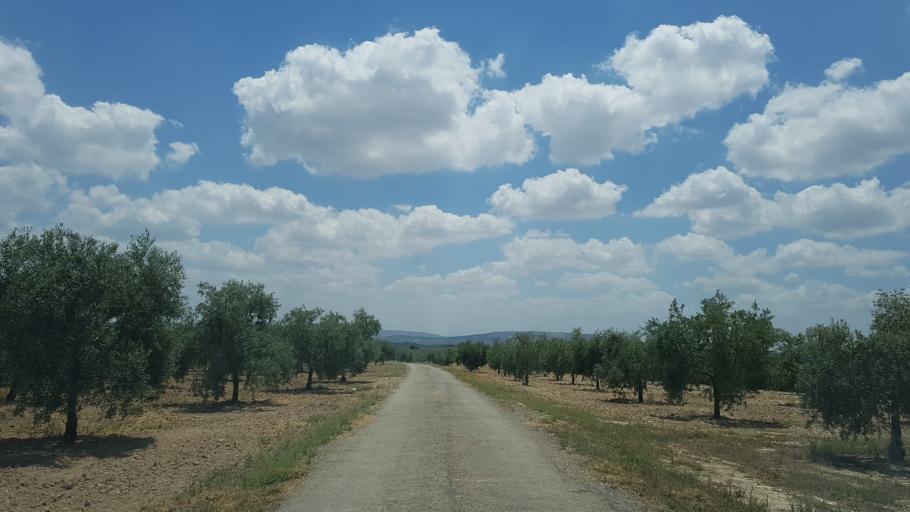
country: ES
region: Andalusia
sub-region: Province of Cordoba
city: Cabra
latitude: 37.5251
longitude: -4.4593
